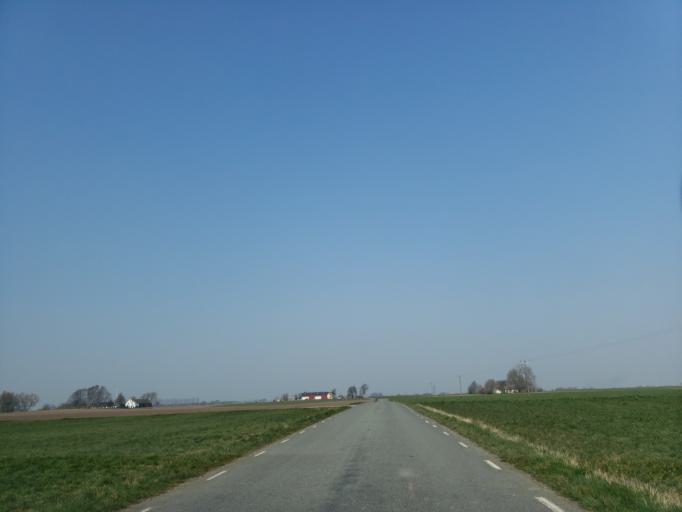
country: SE
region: Skane
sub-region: Simrishamns Kommun
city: Simrishamn
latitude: 55.4530
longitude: 14.2150
